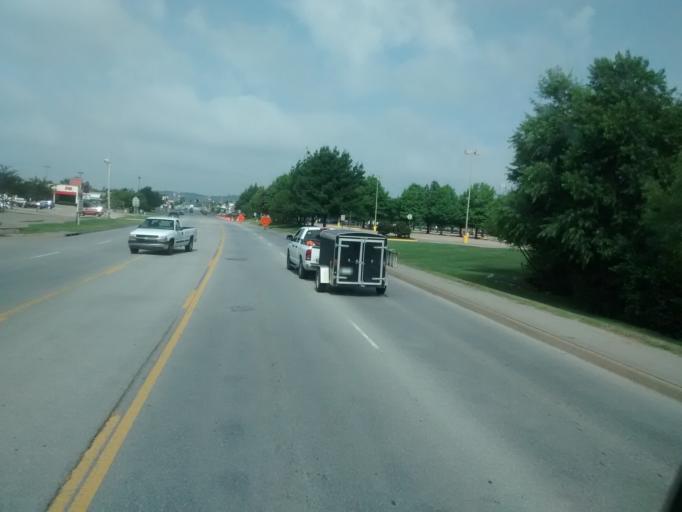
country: US
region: Arkansas
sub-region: Washington County
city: Fayetteville
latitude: 36.0568
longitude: -94.1764
